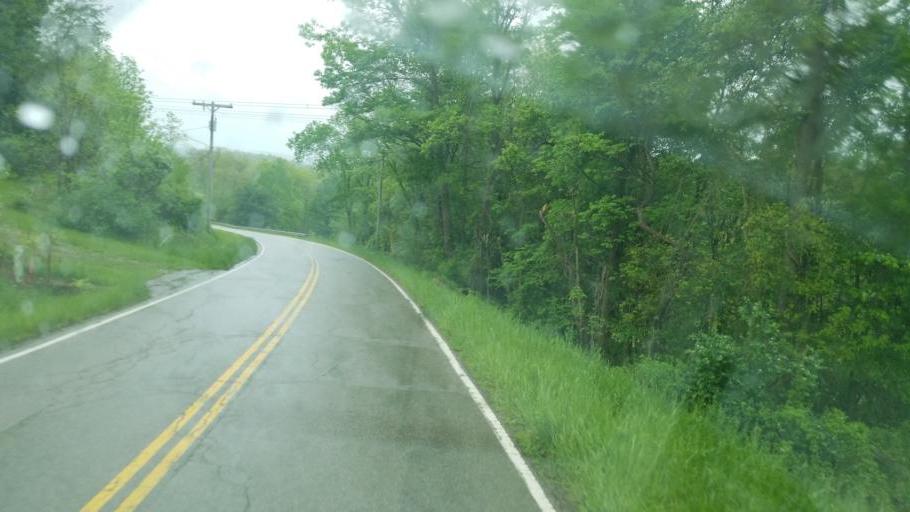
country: US
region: Ohio
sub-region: Muskingum County
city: Frazeysburg
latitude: 40.0989
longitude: -82.0976
